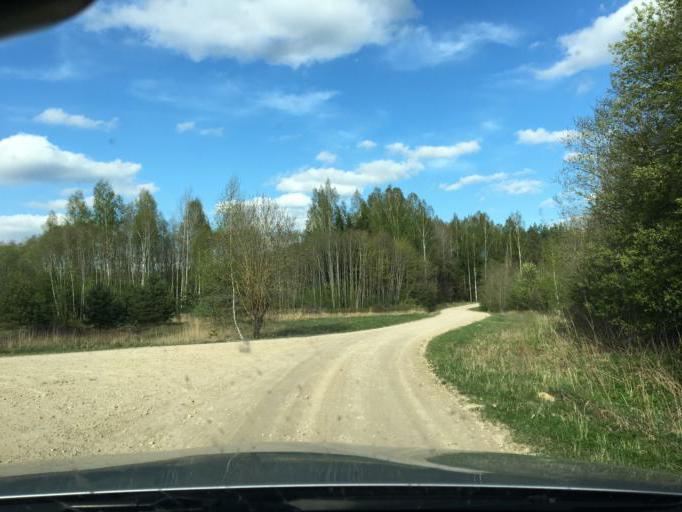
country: LV
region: Ozolnieku
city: Ozolnieki
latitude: 56.6683
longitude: 23.8810
